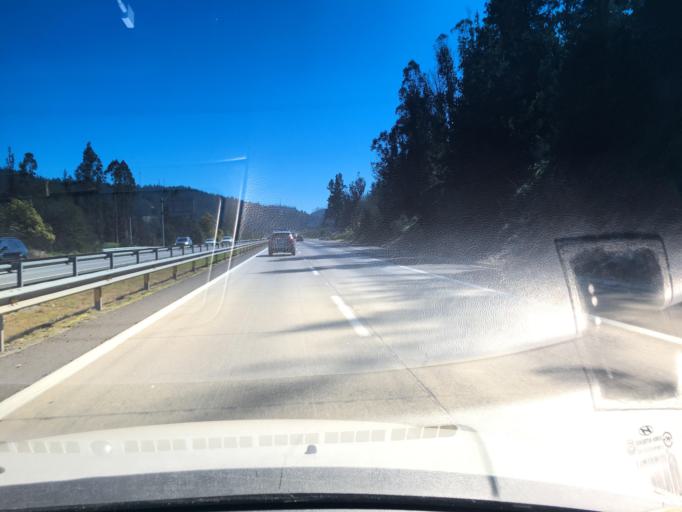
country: CL
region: Valparaiso
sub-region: Provincia de Marga Marga
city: Quilpue
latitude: -33.2327
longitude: -71.4633
